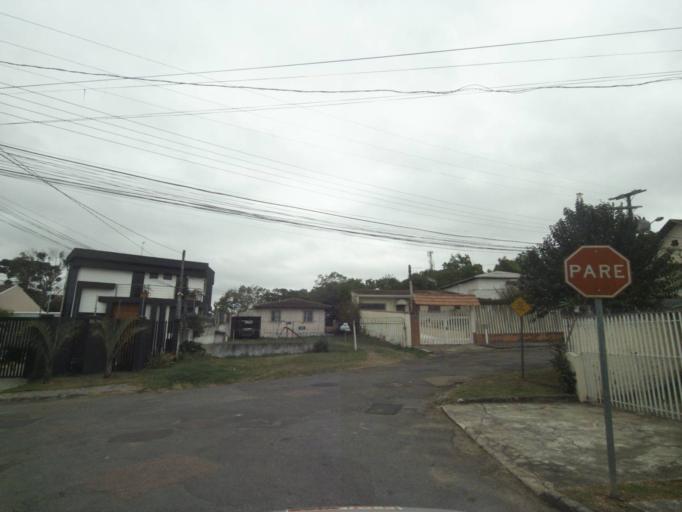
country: BR
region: Parana
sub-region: Sao Jose Dos Pinhais
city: Sao Jose dos Pinhais
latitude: -25.4866
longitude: -49.2250
